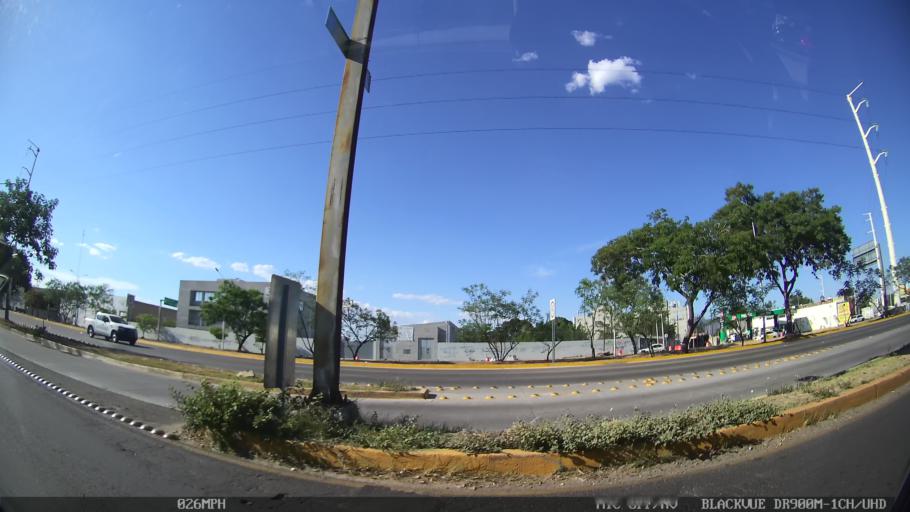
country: MX
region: Jalisco
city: Tlaquepaque
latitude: 20.7143
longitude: -103.3038
